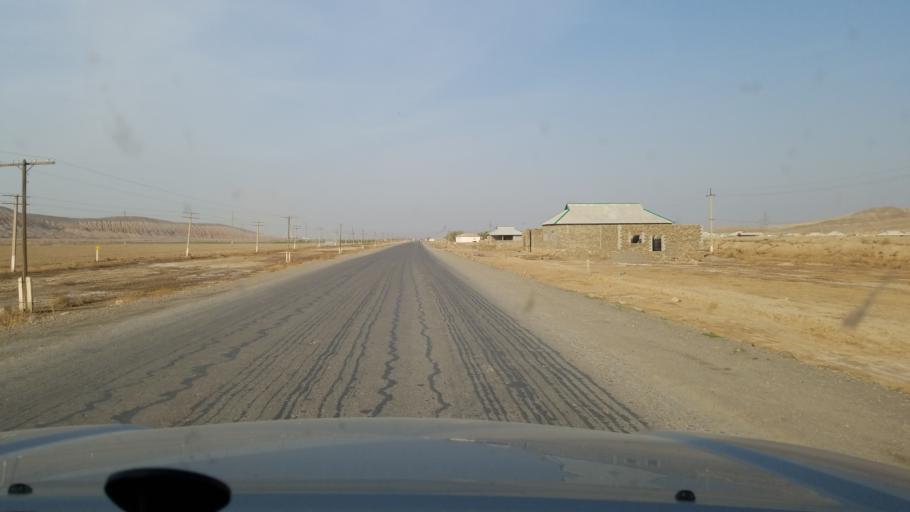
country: AF
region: Jowzjan
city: Qarqin
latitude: 37.5285
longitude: 66.0539
